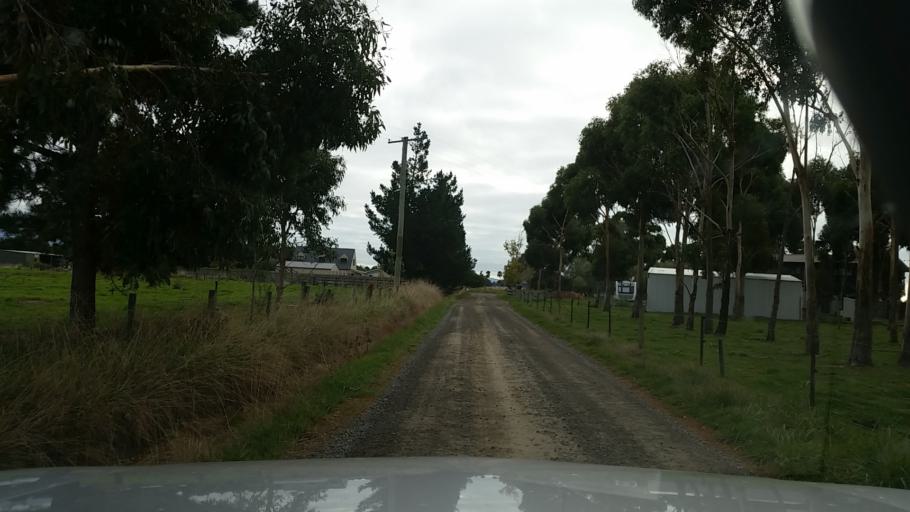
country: NZ
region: Marlborough
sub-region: Marlborough District
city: Blenheim
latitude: -41.5207
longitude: 174.0392
